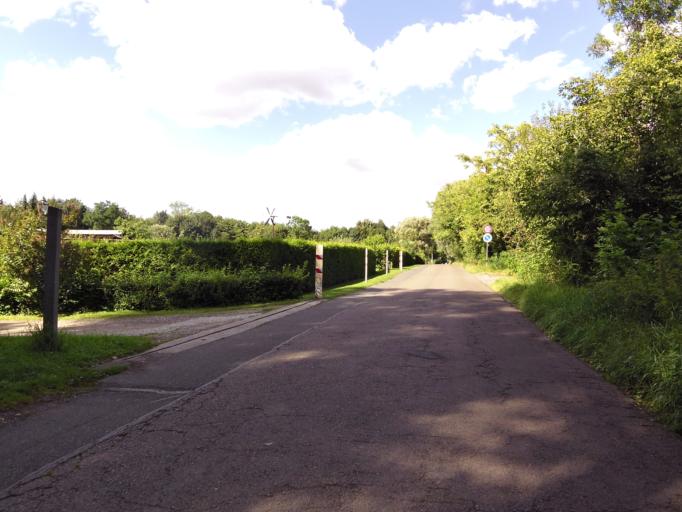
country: DE
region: Saxony
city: Markkleeberg
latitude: 51.2883
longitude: 12.4024
